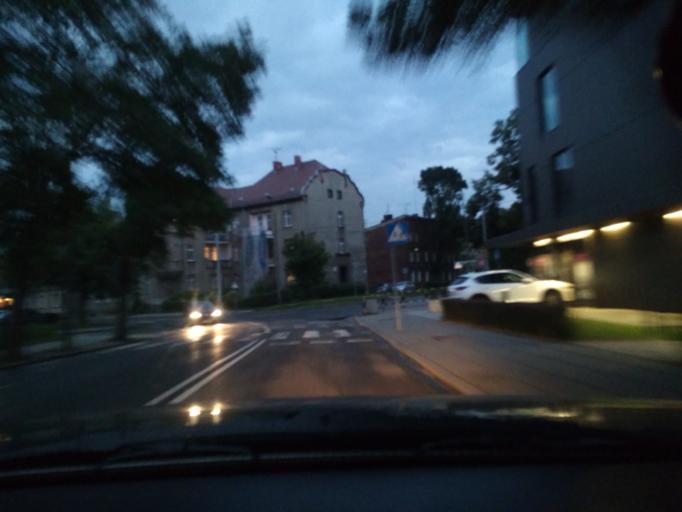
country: PL
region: Silesian Voivodeship
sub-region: Gliwice
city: Gliwice
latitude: 50.2892
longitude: 18.6556
